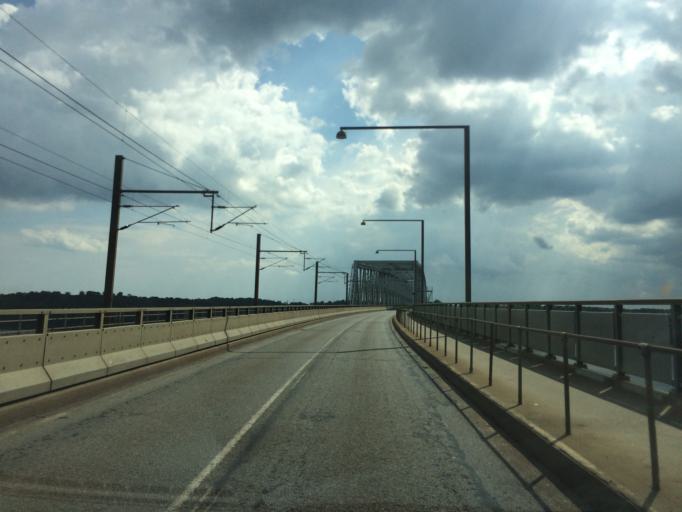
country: DK
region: South Denmark
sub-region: Fredericia Kommune
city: Snoghoj
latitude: 55.5219
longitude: 9.7145
